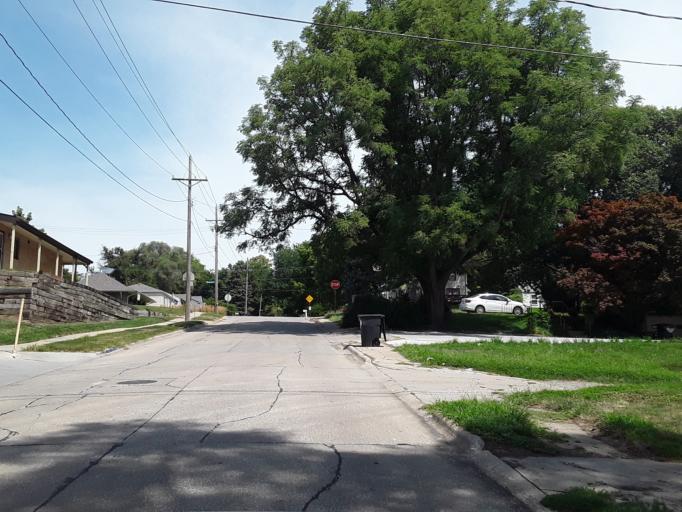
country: US
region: Nebraska
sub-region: Sarpy County
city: Bellevue
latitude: 41.1358
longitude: -95.9042
